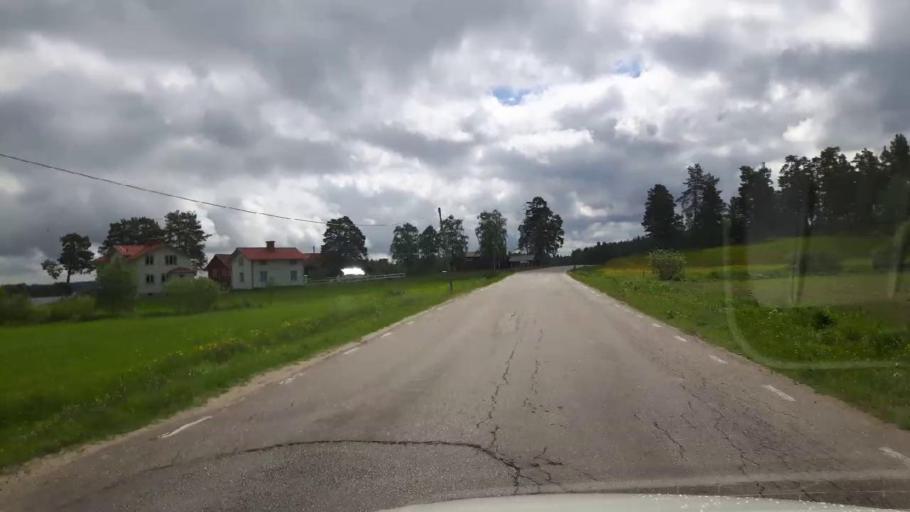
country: SE
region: Gaevleborg
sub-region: Ovanakers Kommun
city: Edsbyn
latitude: 61.3475
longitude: 15.9242
